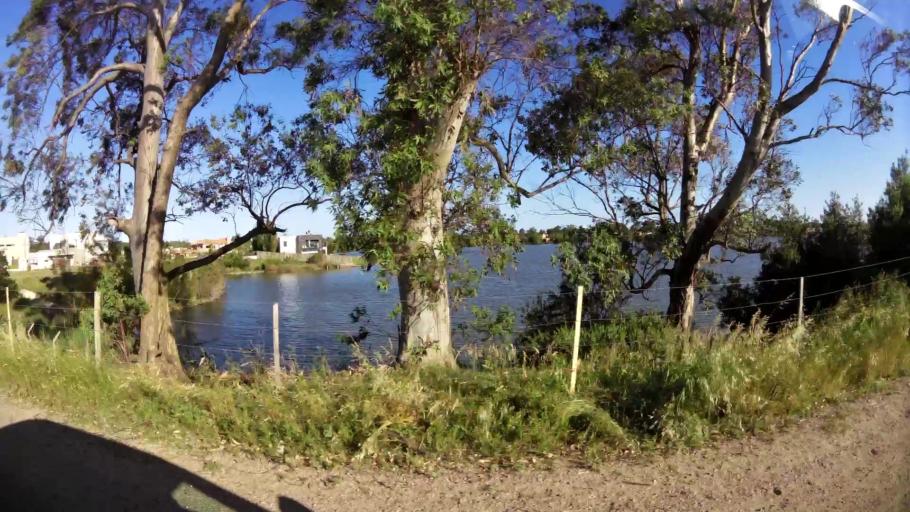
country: UY
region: Canelones
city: Paso de Carrasco
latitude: -34.8618
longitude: -56.0414
